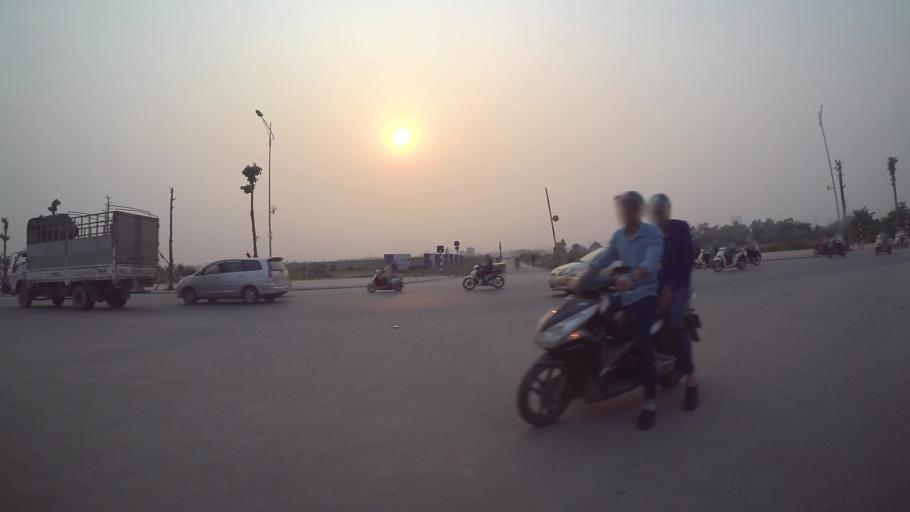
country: VN
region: Ha Noi
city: Ha Dong
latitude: 20.9412
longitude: 105.7845
